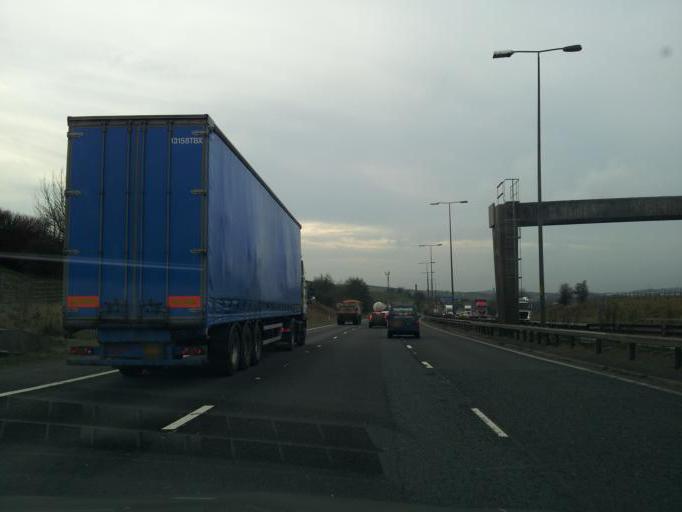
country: GB
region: England
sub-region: Borough of Rochdale
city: Milnrow
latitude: 53.6093
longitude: -2.0932
